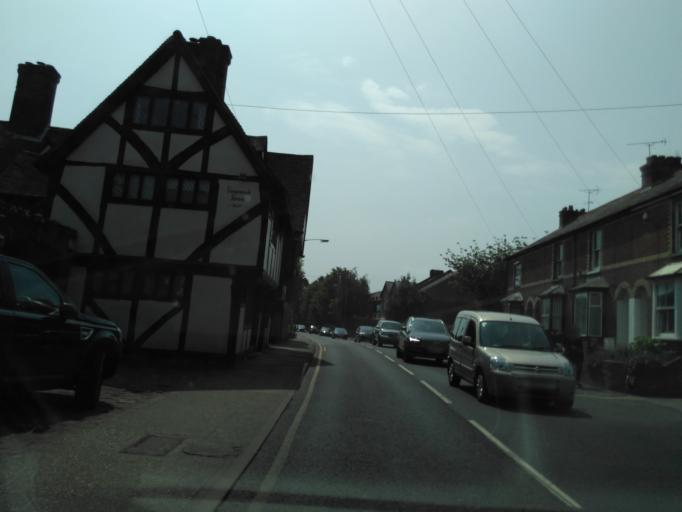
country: GB
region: England
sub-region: Kent
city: Canterbury
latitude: 51.2862
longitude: 1.0813
